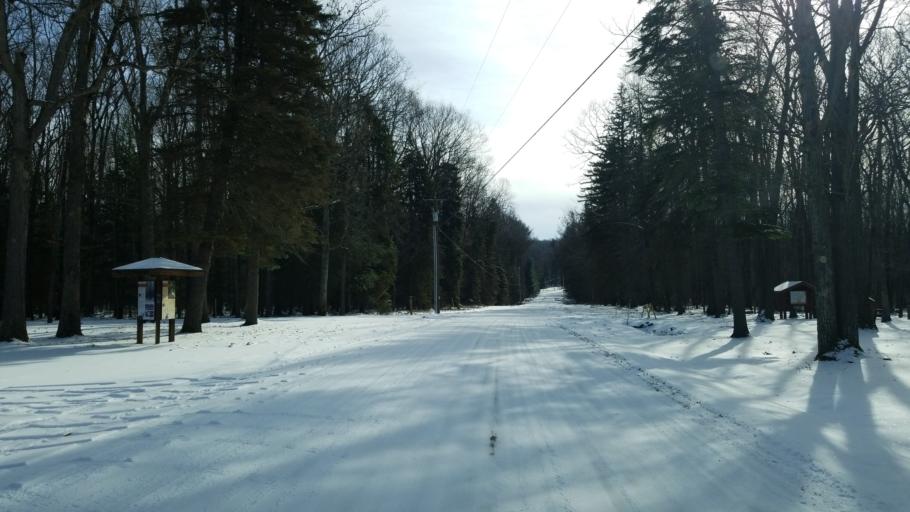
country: US
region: Pennsylvania
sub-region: Clearfield County
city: Clearfield
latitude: 41.1129
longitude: -78.5261
